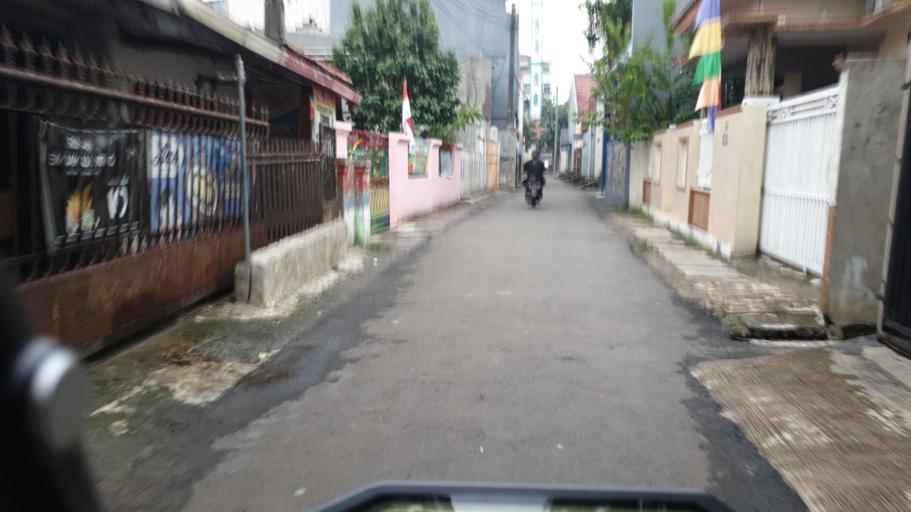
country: ID
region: West Java
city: Depok
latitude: -6.3433
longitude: 106.8237
